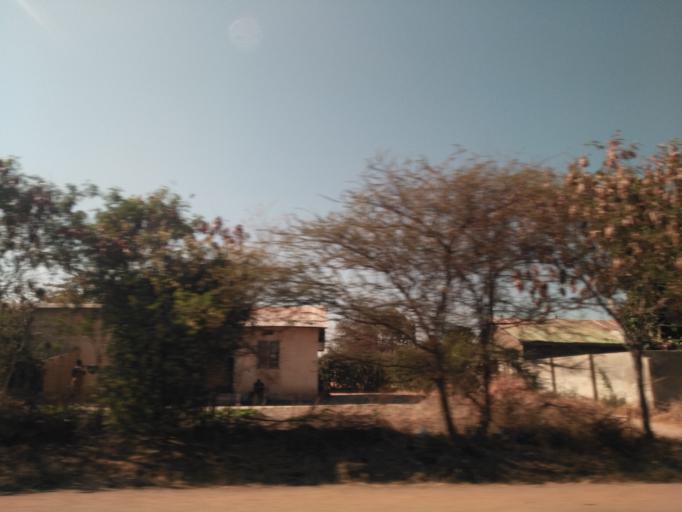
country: TZ
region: Dodoma
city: Dodoma
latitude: -6.1592
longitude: 35.7503
